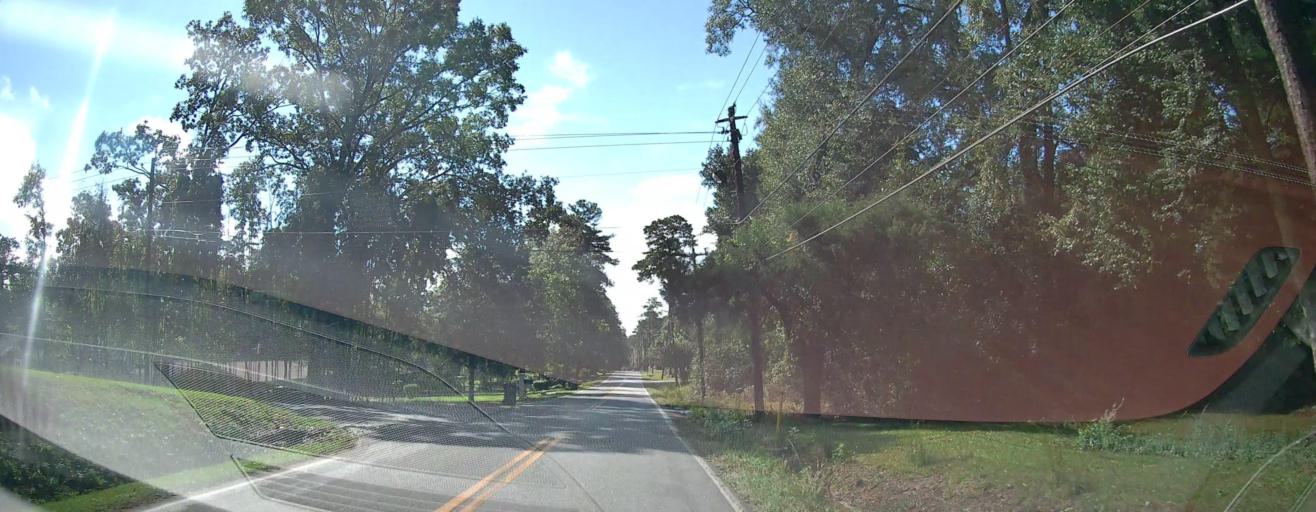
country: US
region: Georgia
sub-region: Bibb County
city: Macon
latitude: 32.8952
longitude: -83.7173
